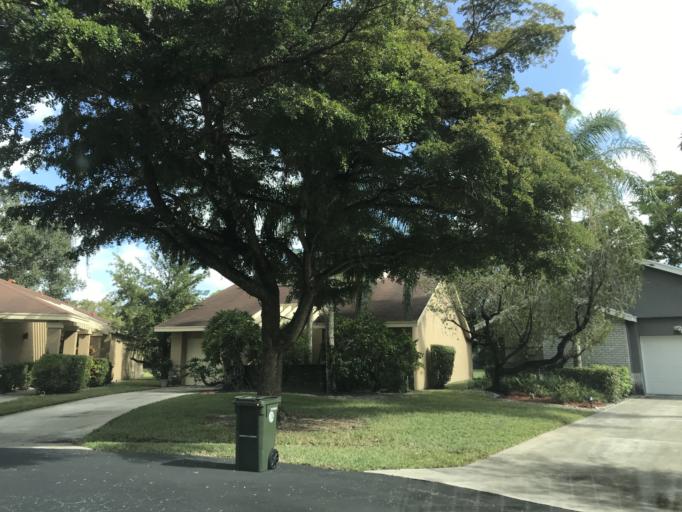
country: US
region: Florida
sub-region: Broward County
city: Coconut Creek
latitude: 26.2625
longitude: -80.1905
